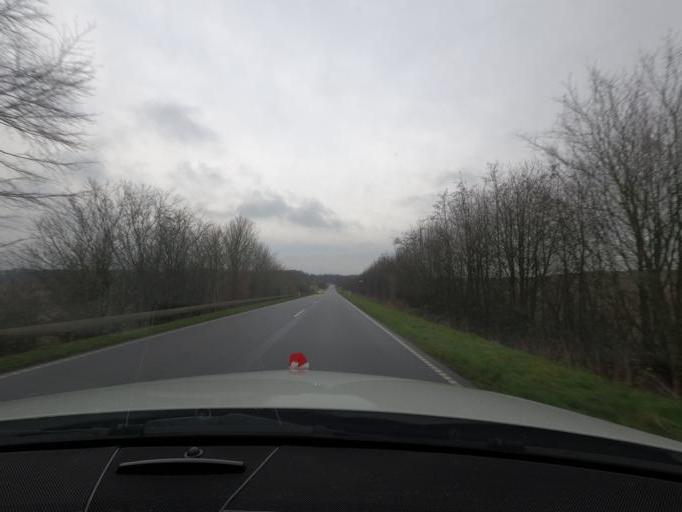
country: DK
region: South Denmark
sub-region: Haderslev Kommune
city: Haderslev
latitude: 55.1835
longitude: 9.4037
